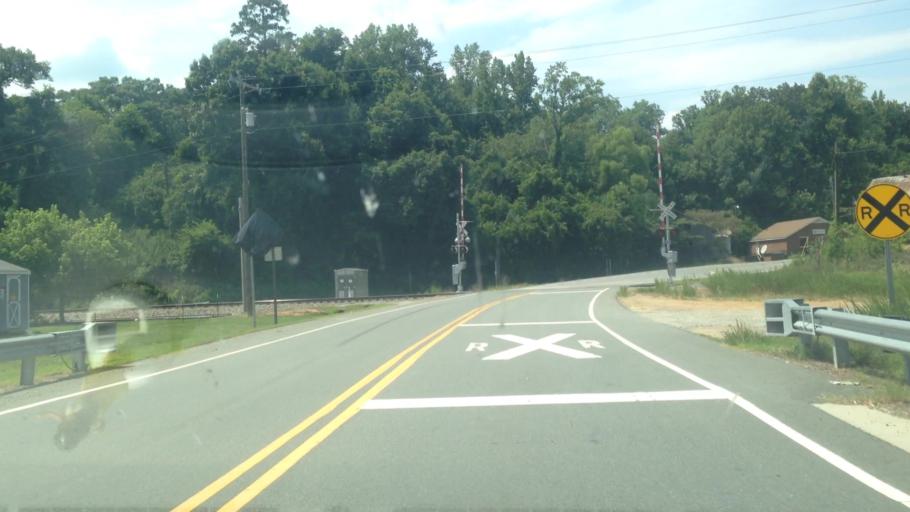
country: US
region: North Carolina
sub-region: Stokes County
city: Walnut Cove
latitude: 36.3196
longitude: -80.0504
